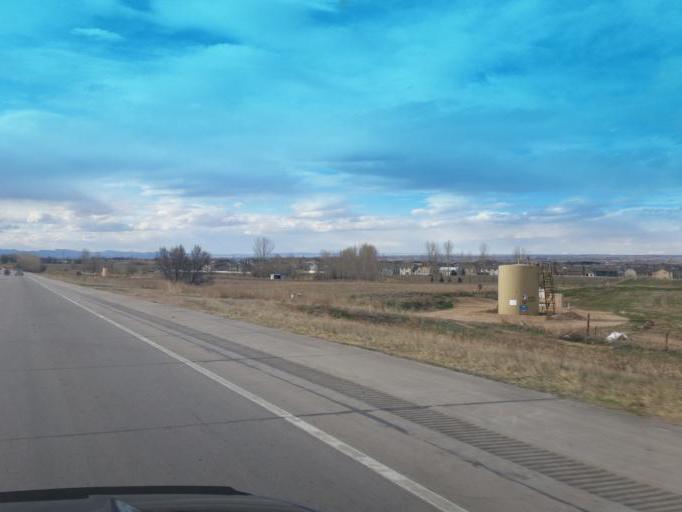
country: US
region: Colorado
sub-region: Weld County
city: Milliken
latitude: 40.3951
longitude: -104.8033
